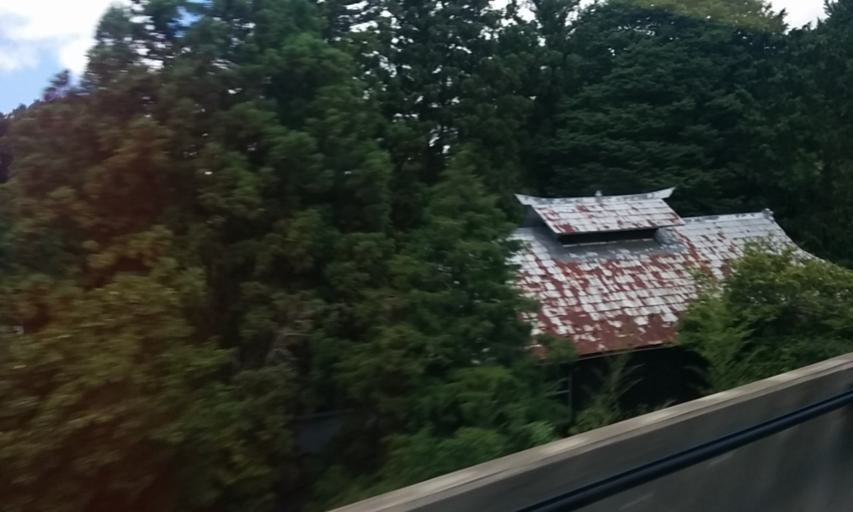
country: JP
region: Fukushima
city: Motomiya
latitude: 37.4822
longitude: 140.4184
